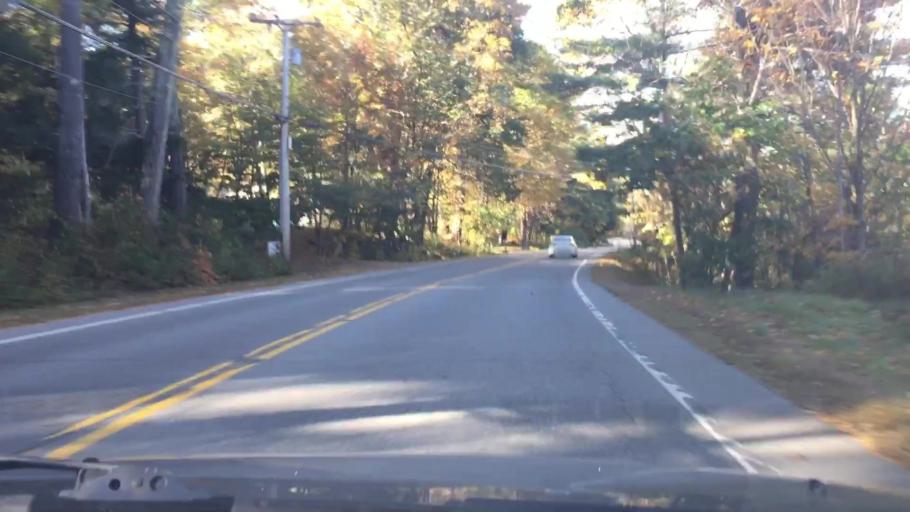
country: US
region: New Hampshire
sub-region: Cheshire County
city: Keene
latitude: 43.0052
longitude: -72.2606
